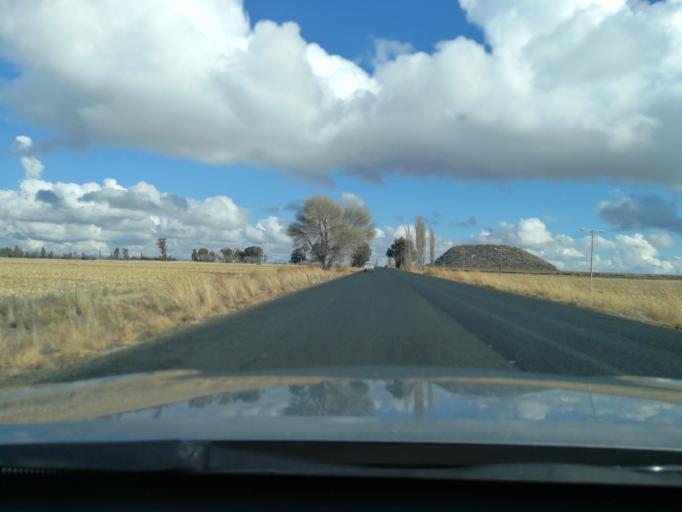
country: ZA
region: Orange Free State
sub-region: Thabo Mofutsanyana District Municipality
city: Reitz
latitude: -27.8906
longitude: 28.3972
